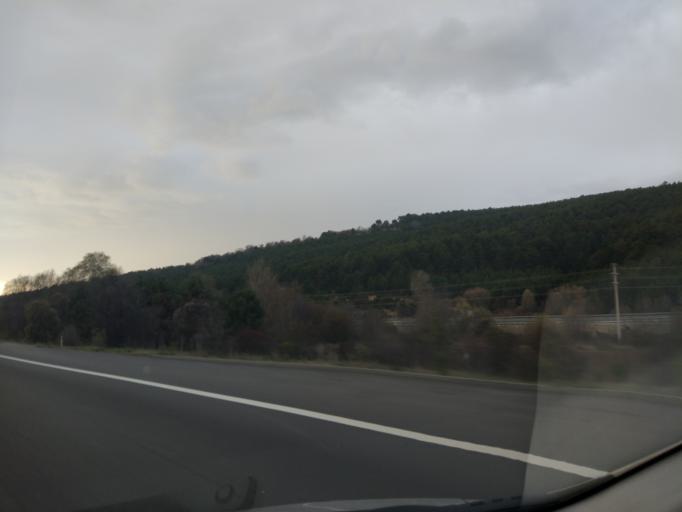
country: TR
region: Bolu
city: Yenicaga
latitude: 40.7428
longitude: 31.8543
